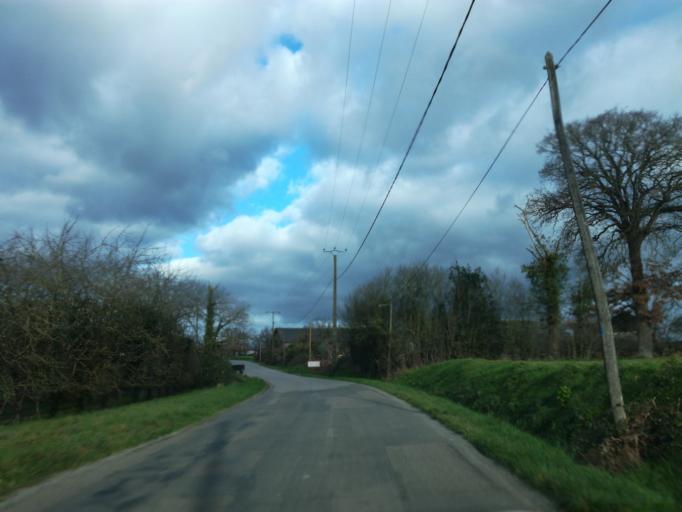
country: FR
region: Brittany
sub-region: Departement d'Ille-et-Vilaine
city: Fouillard
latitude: 48.1464
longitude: -1.5751
